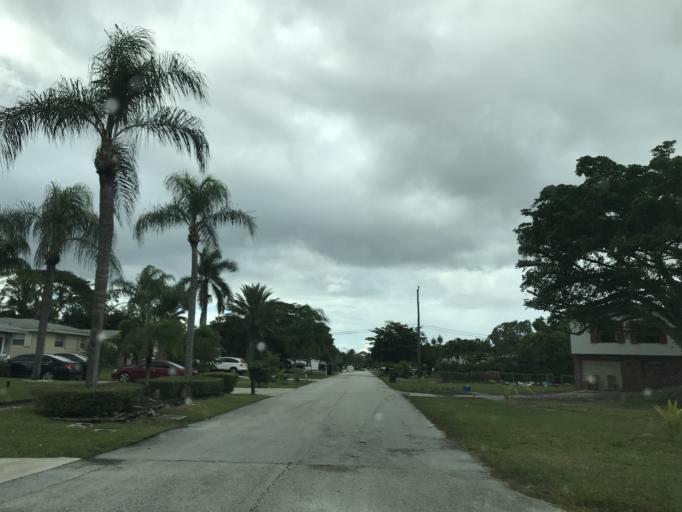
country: US
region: Florida
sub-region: Palm Beach County
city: Delray Beach
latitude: 26.4698
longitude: -80.0982
